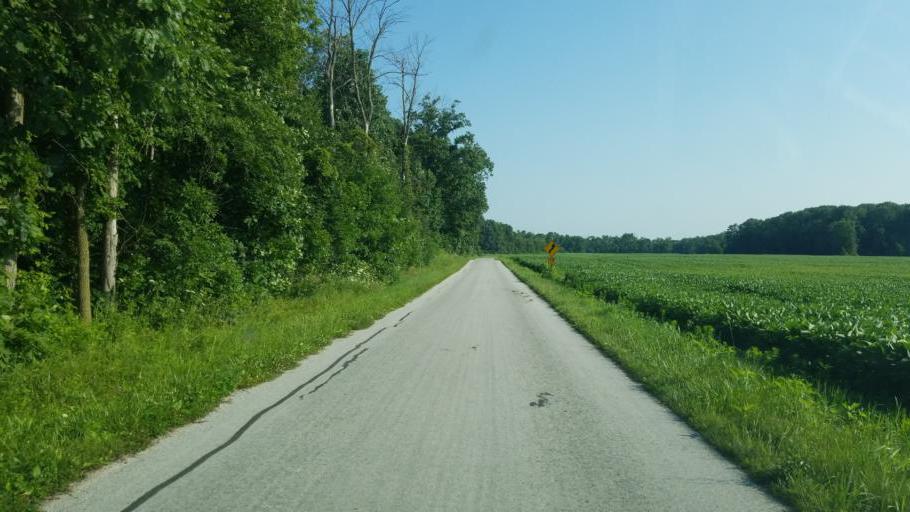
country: US
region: Ohio
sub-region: Hardin County
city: Kenton
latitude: 40.6011
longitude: -83.5424
